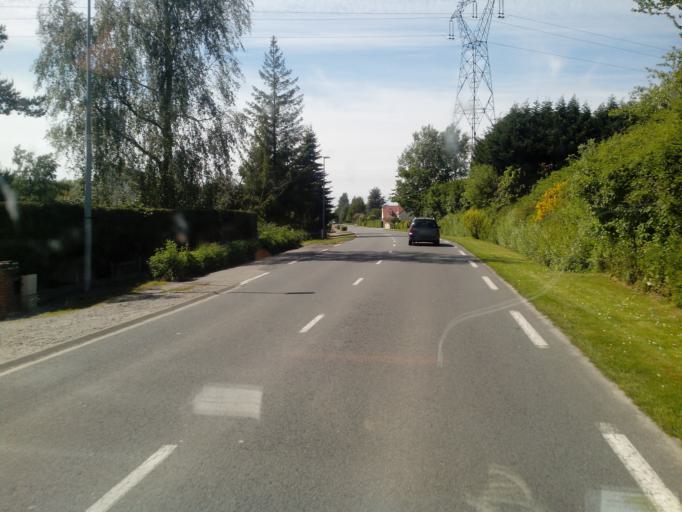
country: FR
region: Nord-Pas-de-Calais
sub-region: Departement du Pas-de-Calais
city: Montreuil
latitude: 50.4919
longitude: 1.7206
